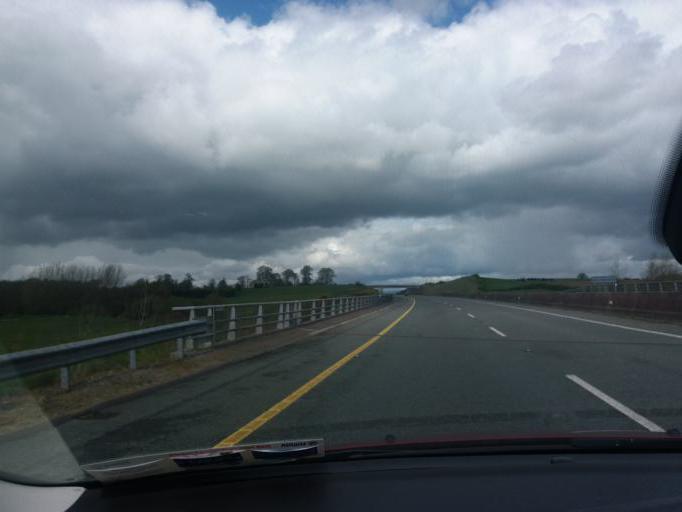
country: IE
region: Leinster
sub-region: Laois
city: Rathdowney
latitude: 52.8189
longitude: -7.4939
